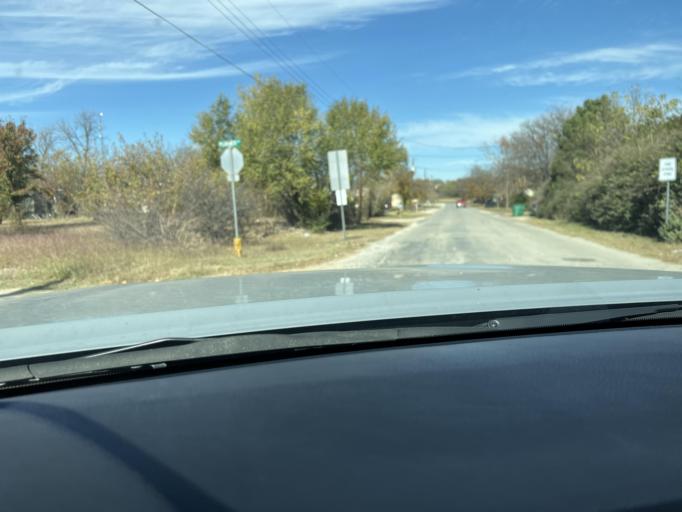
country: US
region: Texas
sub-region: Eastland County
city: Eastland
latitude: 32.3995
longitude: -98.8307
